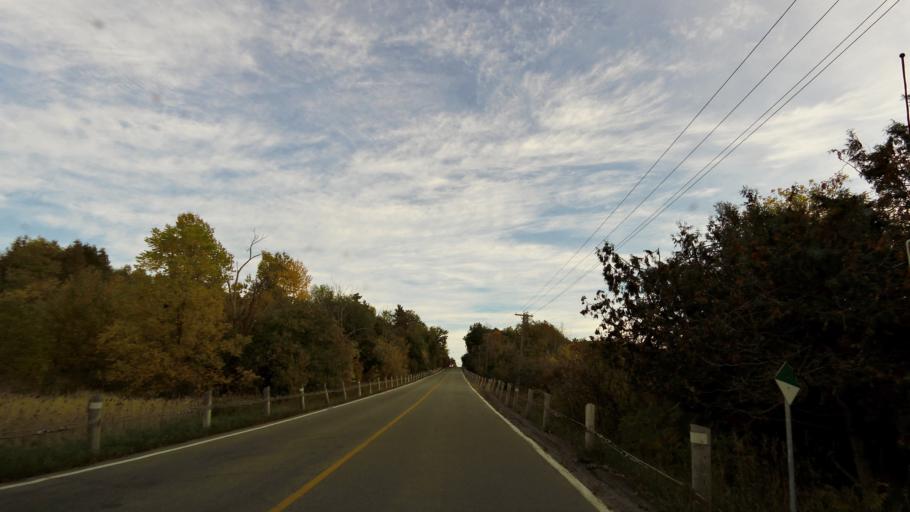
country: CA
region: Ontario
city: Brampton
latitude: 43.7080
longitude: -79.9335
